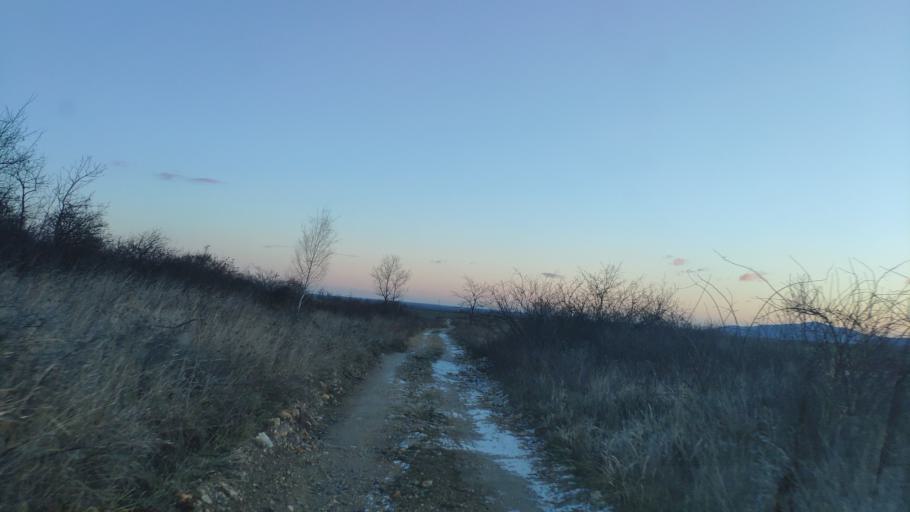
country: HU
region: Borsod-Abauj-Zemplen
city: Olaszliszka
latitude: 48.2691
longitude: 21.4000
